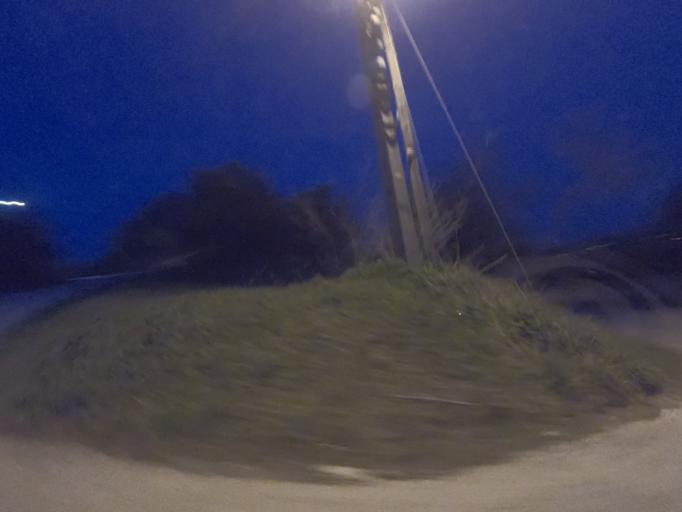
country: PT
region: Setubal
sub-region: Palmela
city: Palmela
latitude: 38.5430
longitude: -8.9120
